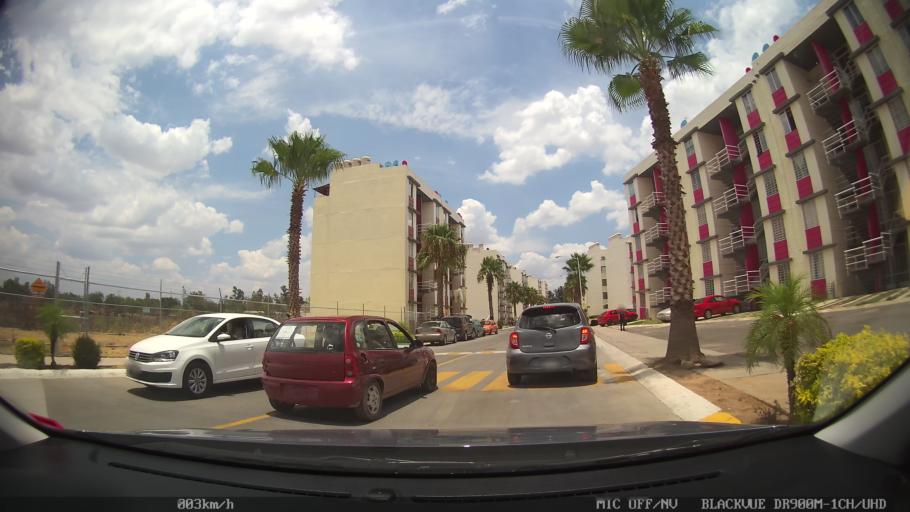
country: MX
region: Jalisco
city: Tonala
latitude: 20.6398
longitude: -103.2269
